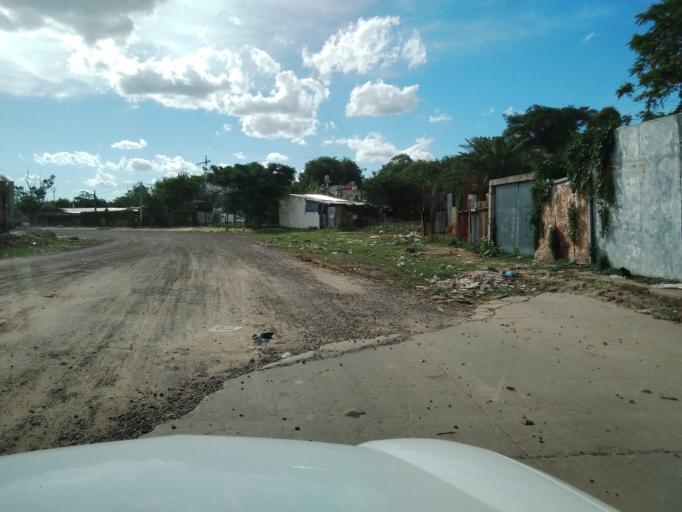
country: AR
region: Corrientes
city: Corrientes
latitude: -27.4812
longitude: -58.8510
